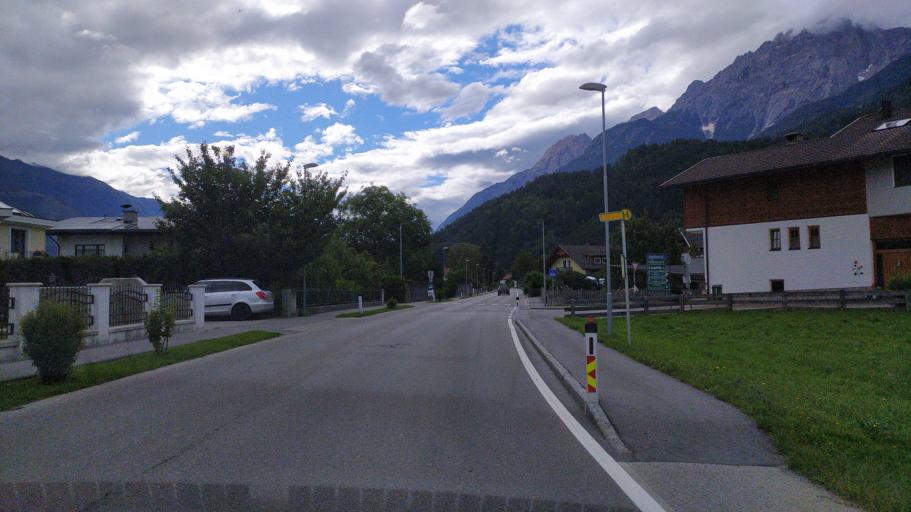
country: AT
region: Tyrol
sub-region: Politischer Bezirk Lienz
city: Tristach
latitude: 46.8188
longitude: 12.7931
